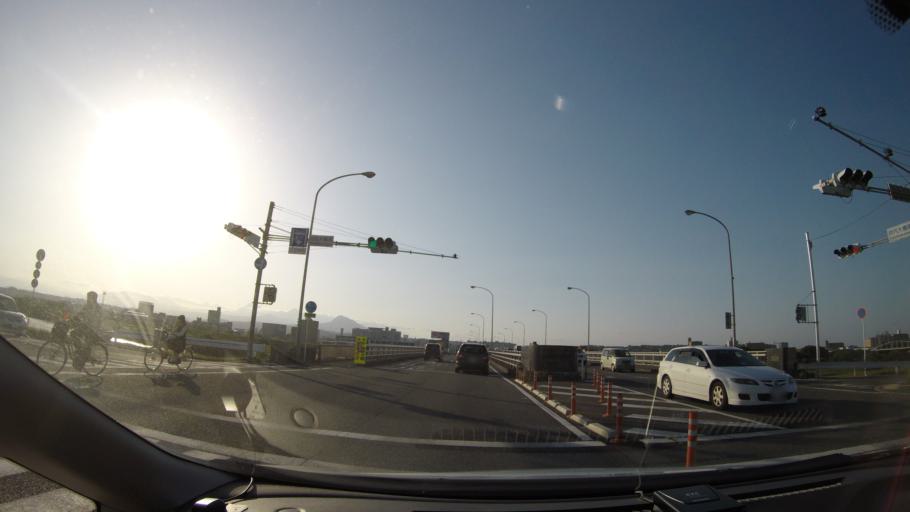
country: JP
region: Oita
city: Oita
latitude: 33.2016
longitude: 131.6062
